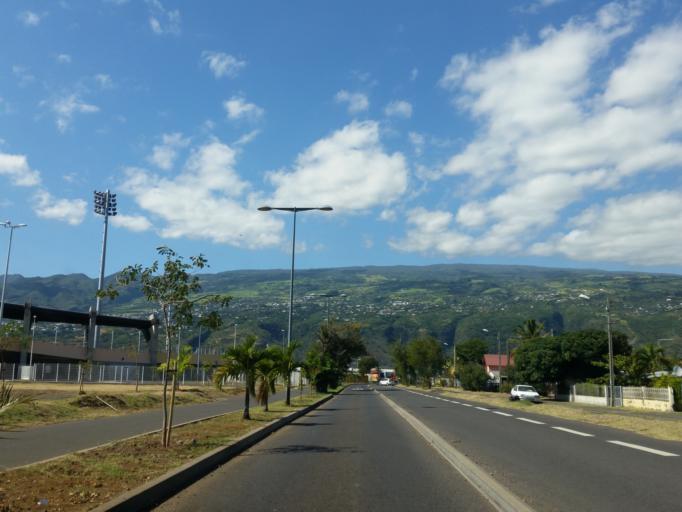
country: RE
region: Reunion
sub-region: Reunion
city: Saint-Paul
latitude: -20.9826
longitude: 55.2881
